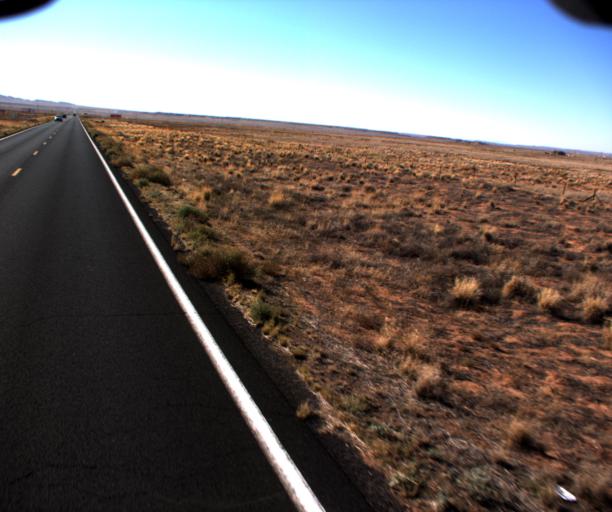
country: US
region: Arizona
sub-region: Navajo County
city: Dilkon
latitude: 35.3754
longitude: -110.4252
